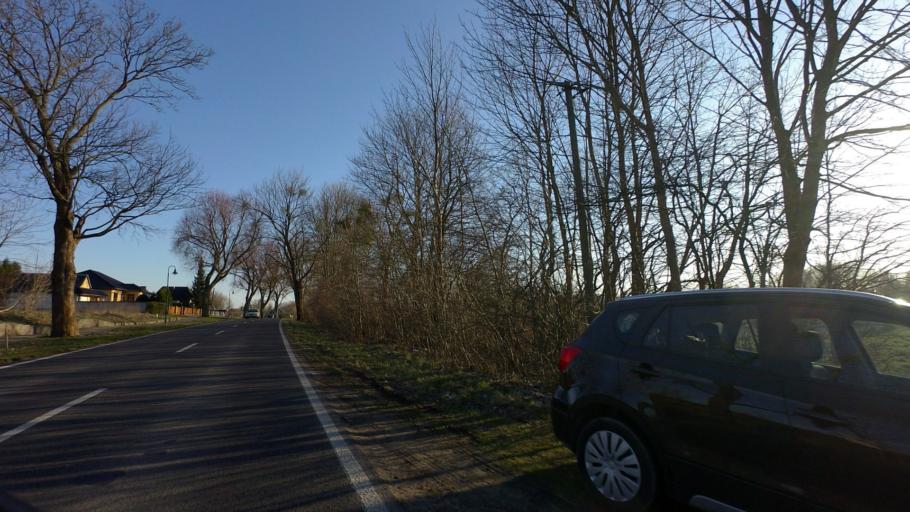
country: DE
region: Brandenburg
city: Eberswalde
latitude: 52.7832
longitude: 13.8391
